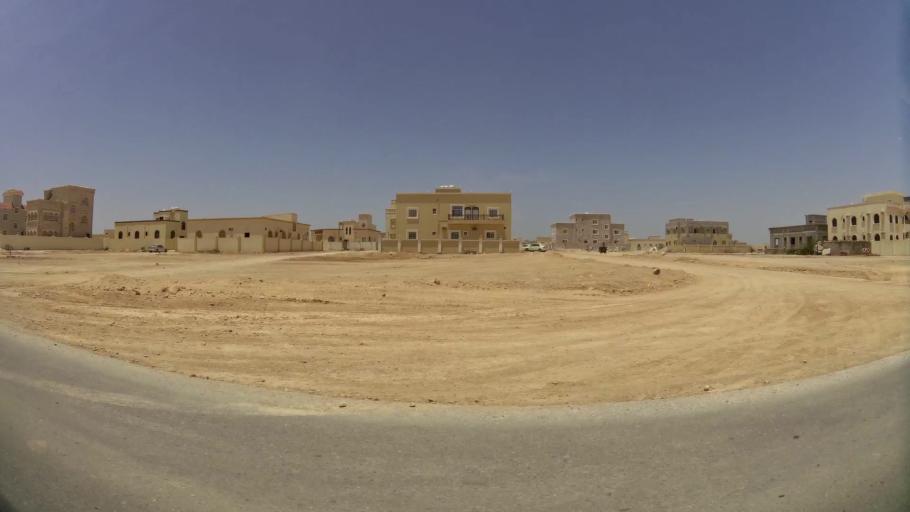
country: OM
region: Zufar
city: Salalah
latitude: 17.0918
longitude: 54.2027
